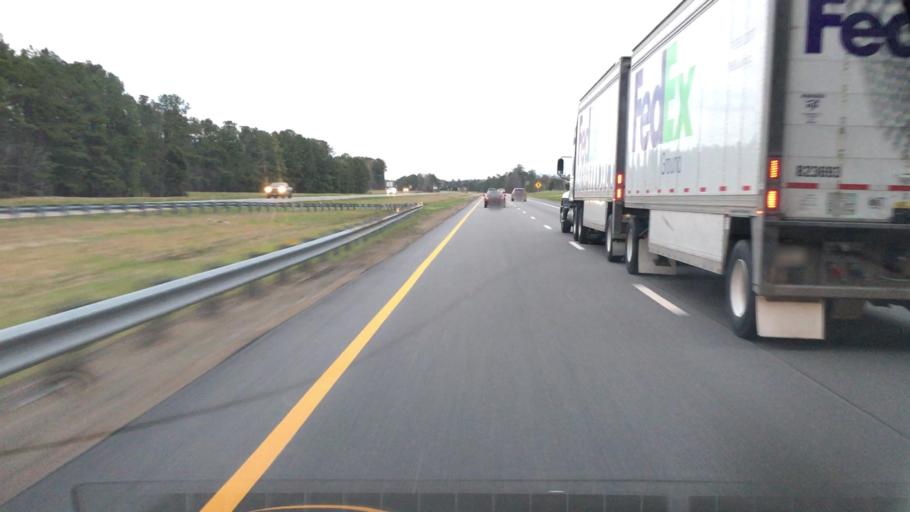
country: US
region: Virginia
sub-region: Sussex County
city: Sussex
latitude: 36.8537
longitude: -77.4241
